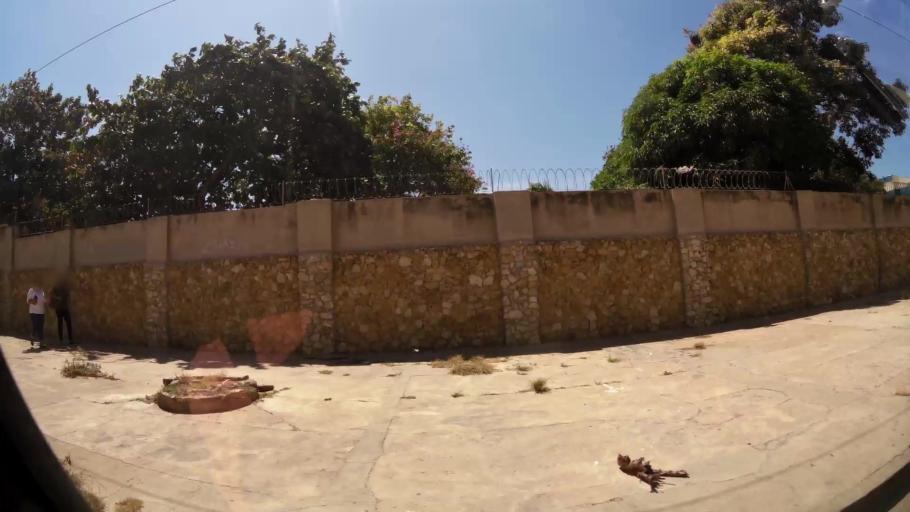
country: CO
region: Atlantico
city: Barranquilla
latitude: 10.9899
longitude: -74.8105
